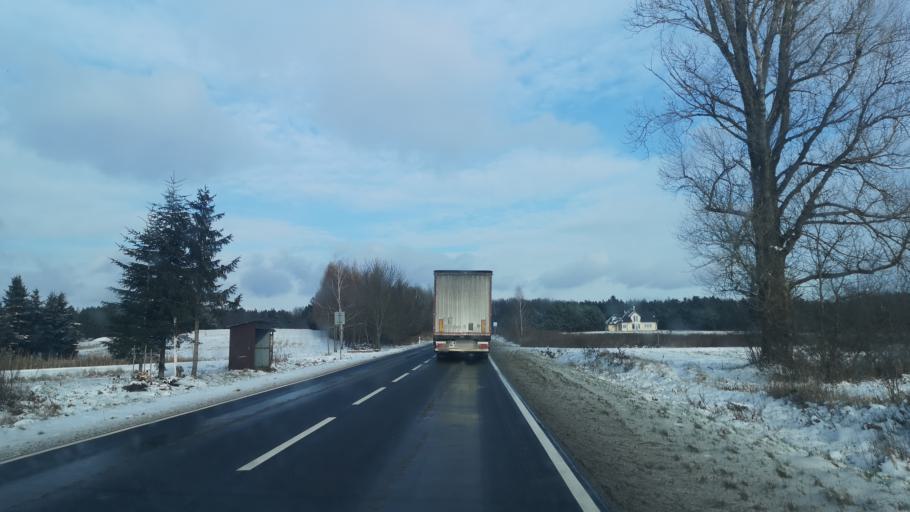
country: PL
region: Subcarpathian Voivodeship
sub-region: Powiat przeworski
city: Sieniawa
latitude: 50.2030
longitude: 22.6348
